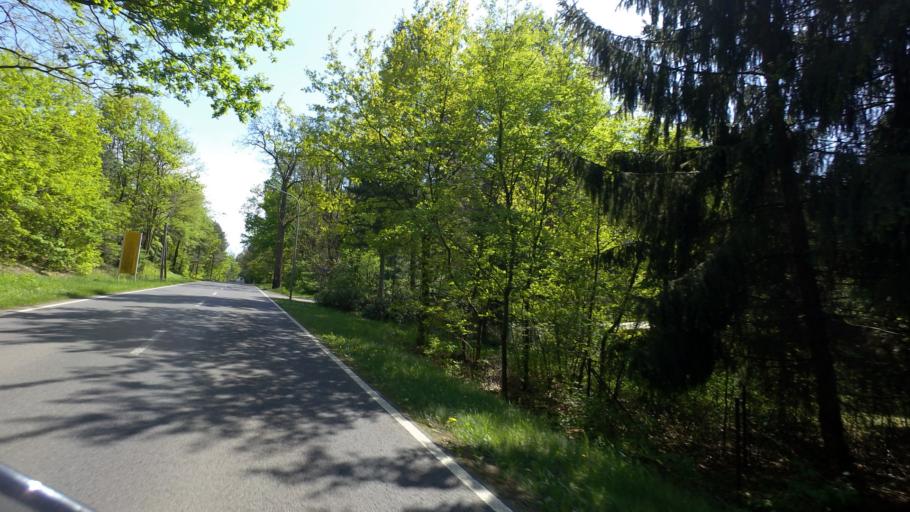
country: DE
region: Brandenburg
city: Lieberose
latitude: 52.0075
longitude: 14.1905
